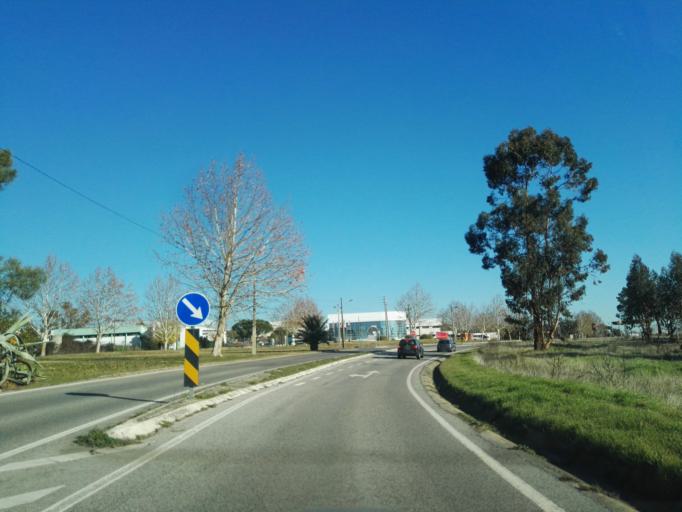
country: PT
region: Santarem
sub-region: Constancia
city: Constancia
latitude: 39.4825
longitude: -8.2912
